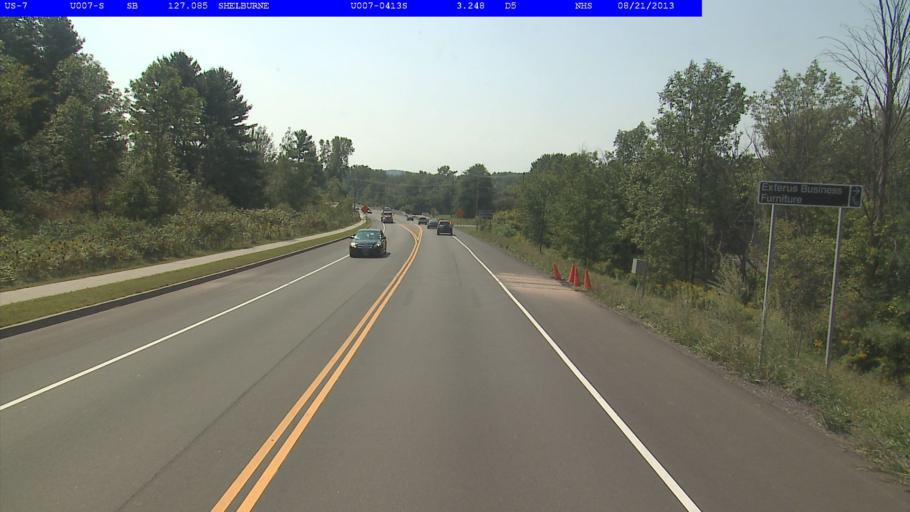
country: US
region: Vermont
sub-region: Chittenden County
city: Burlington
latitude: 44.3892
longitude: -73.2235
